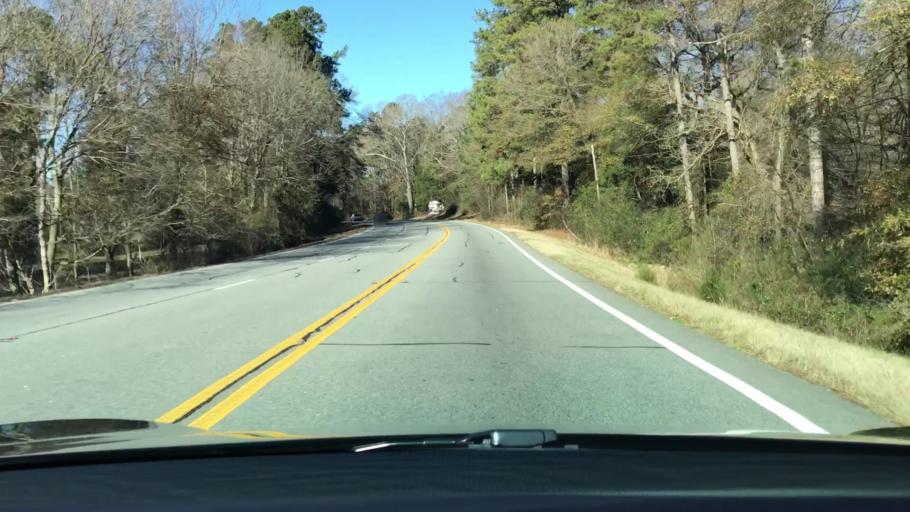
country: US
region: Georgia
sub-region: Barrow County
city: Russell
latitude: 33.8934
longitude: -83.7208
